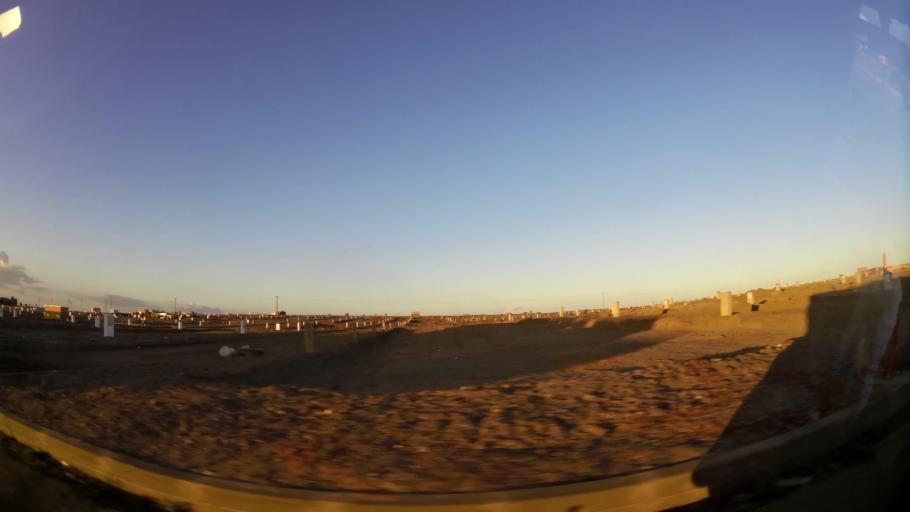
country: MA
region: Marrakech-Tensift-Al Haouz
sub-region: Kelaa-Des-Sraghna
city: Sidi Abdallah
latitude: 32.2416
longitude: -7.9372
